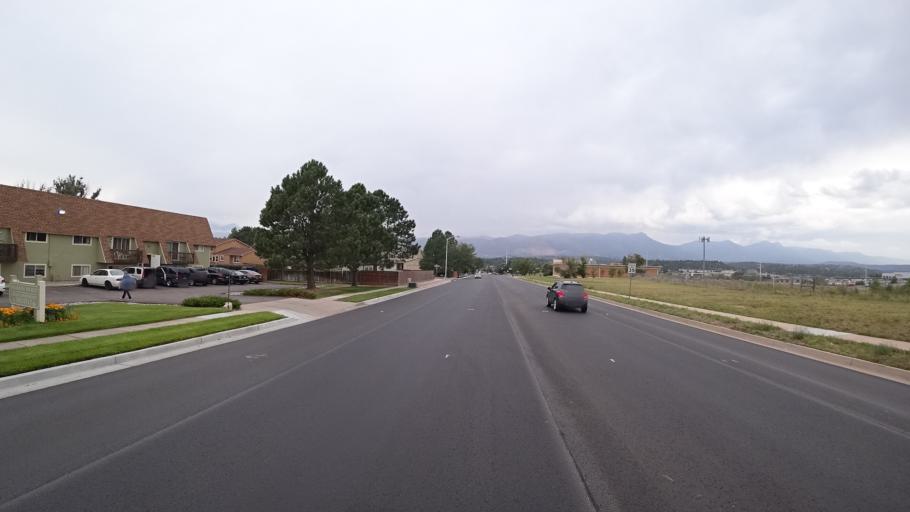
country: US
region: Colorado
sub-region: El Paso County
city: Air Force Academy
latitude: 38.9258
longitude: -104.8069
